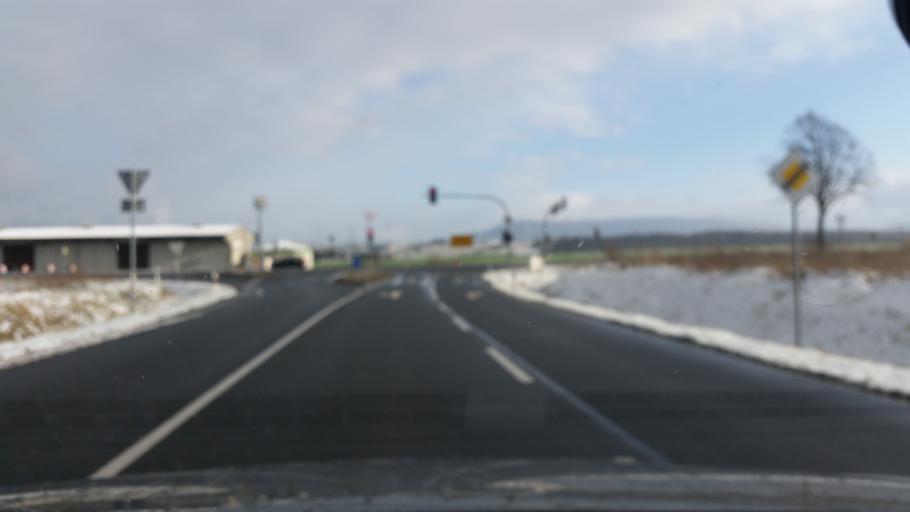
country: DE
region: Lower Saxony
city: Bad Munder am Deister
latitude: 52.1424
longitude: 9.4451
